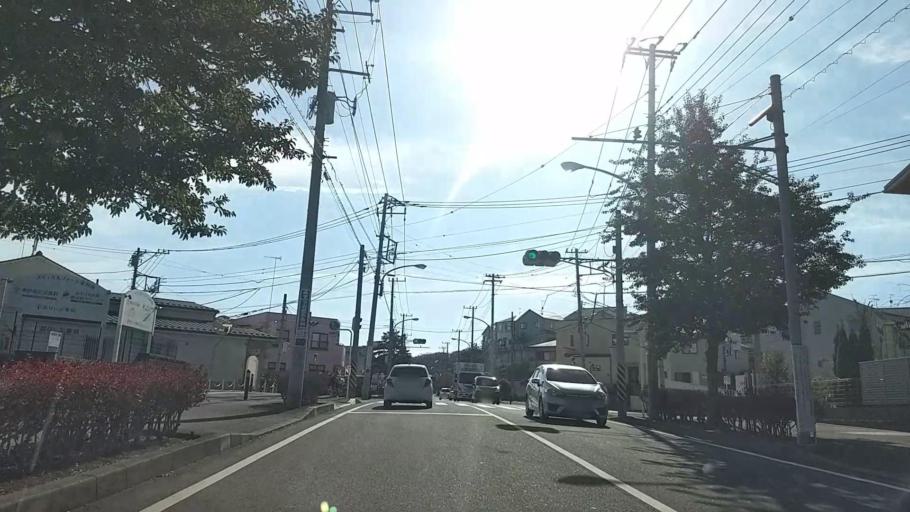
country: JP
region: Kanagawa
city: Hadano
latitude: 35.3642
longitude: 139.2266
